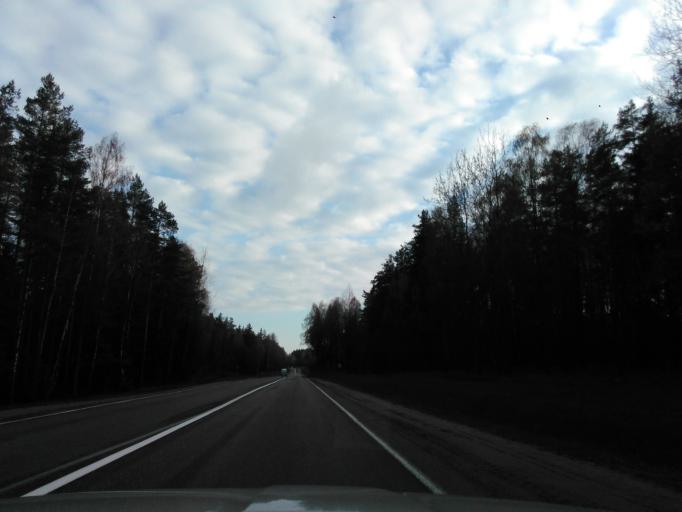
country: BY
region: Minsk
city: Plyeshchanitsy
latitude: 54.3398
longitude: 27.8777
